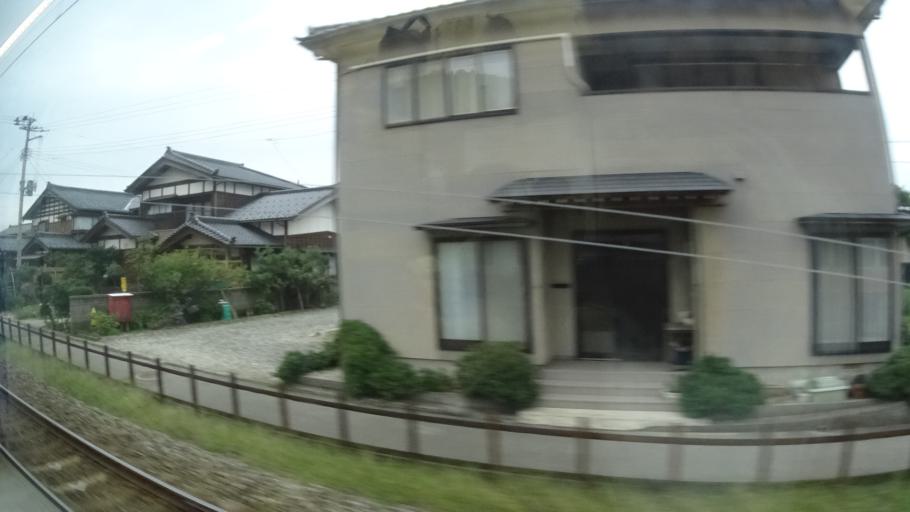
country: JP
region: Niigata
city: Murakami
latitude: 38.4513
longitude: 139.4933
